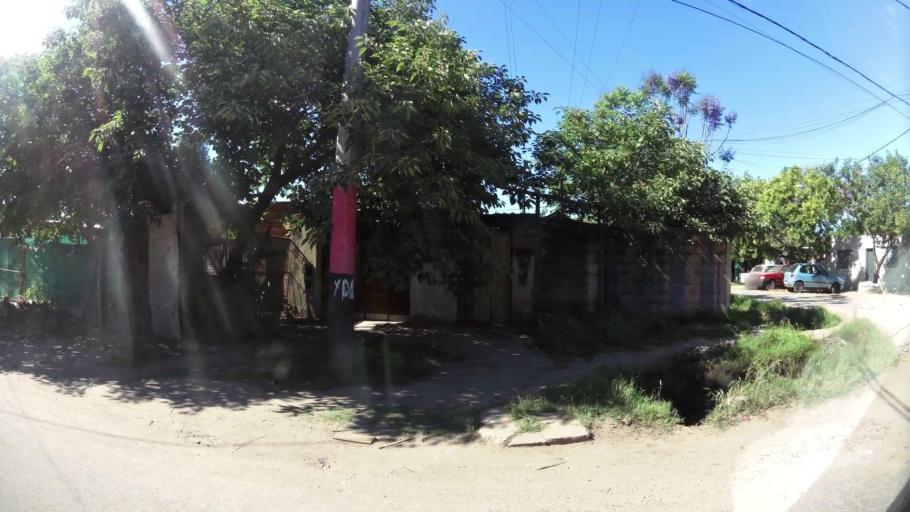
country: AR
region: Santa Fe
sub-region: Departamento de Rosario
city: Rosario
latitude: -32.9540
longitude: -60.6916
